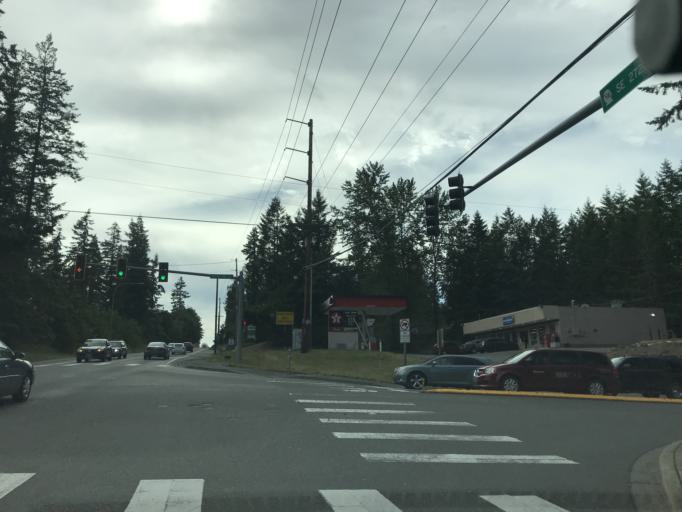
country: US
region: Washington
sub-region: King County
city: Maple Valley
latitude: 47.3581
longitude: -122.0432
